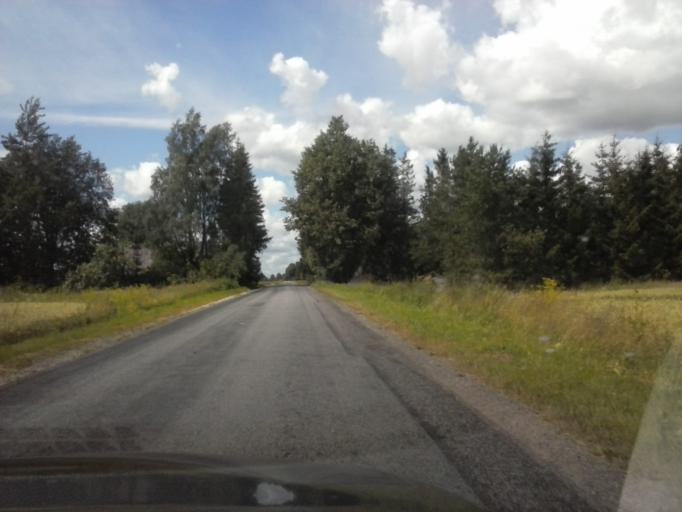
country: EE
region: Laeaene-Virumaa
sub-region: Rakke vald
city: Rakke
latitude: 59.0514
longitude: 26.3667
